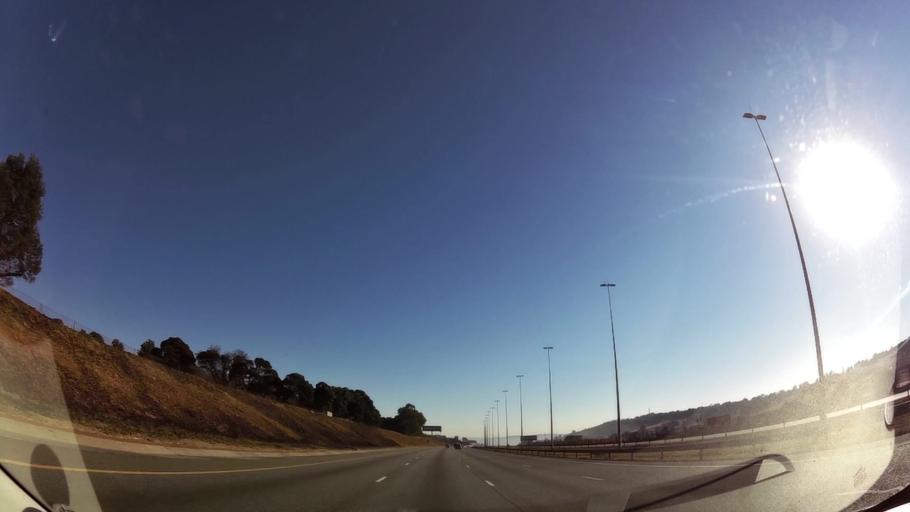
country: ZA
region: Gauteng
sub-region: City of Tshwane Metropolitan Municipality
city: Centurion
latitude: -25.9034
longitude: 28.2551
